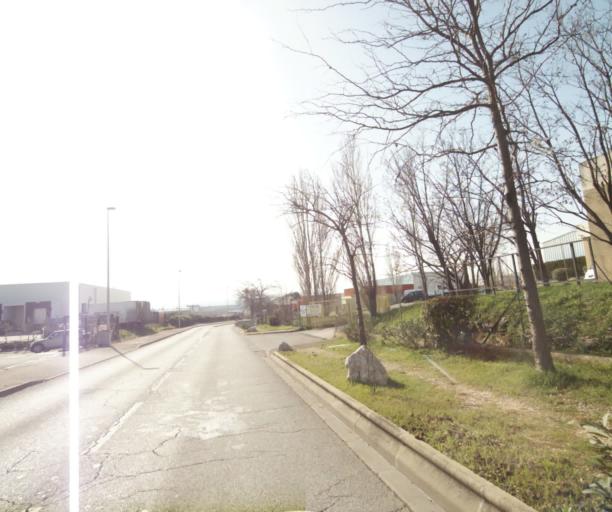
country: FR
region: Provence-Alpes-Cote d'Azur
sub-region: Departement des Bouches-du-Rhone
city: Saint-Victoret
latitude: 43.4337
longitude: 5.2426
